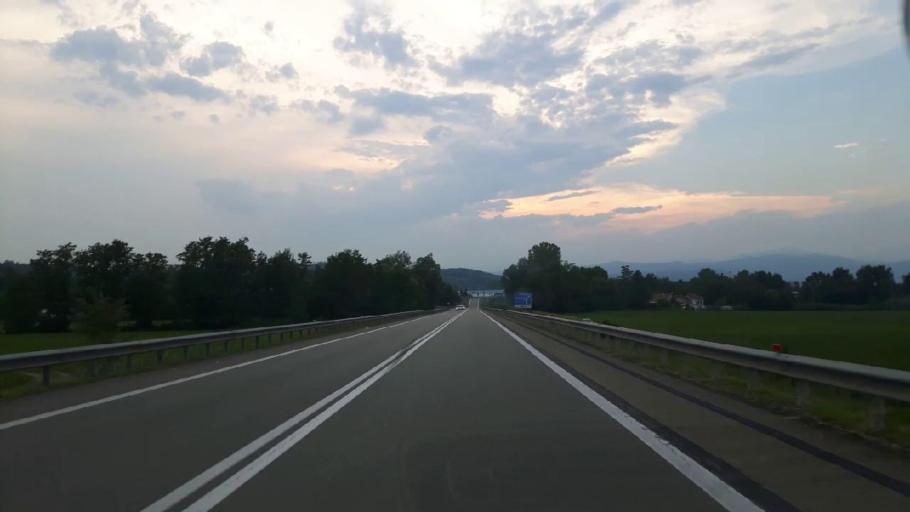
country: IT
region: Piedmont
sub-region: Provincia di Novara
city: Borgo Ticino
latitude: 45.7132
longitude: 8.5973
